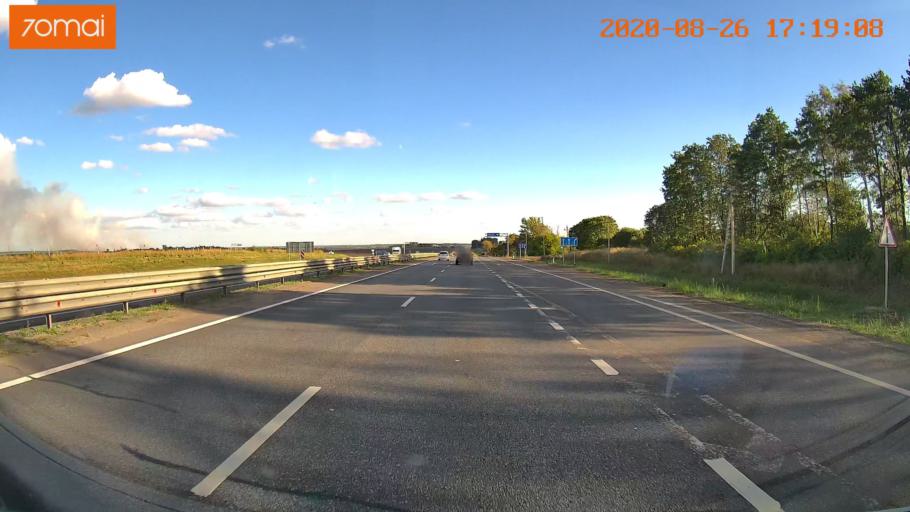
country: RU
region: Tula
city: Volovo
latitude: 53.5993
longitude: 38.1022
